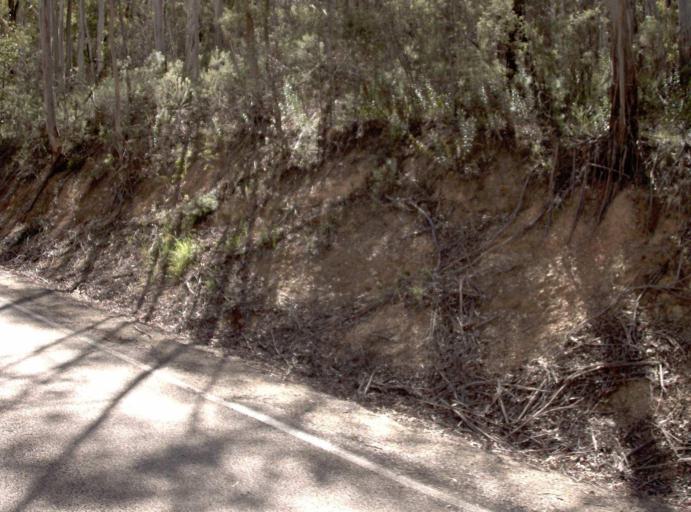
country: AU
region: New South Wales
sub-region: Bombala
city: Bombala
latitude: -37.1624
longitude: 148.7198
